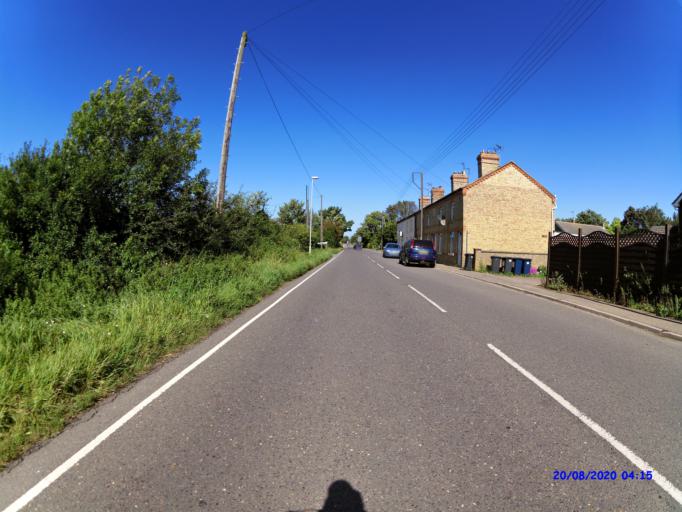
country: GB
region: England
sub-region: Cambridgeshire
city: Ramsey
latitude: 52.4858
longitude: -0.1098
